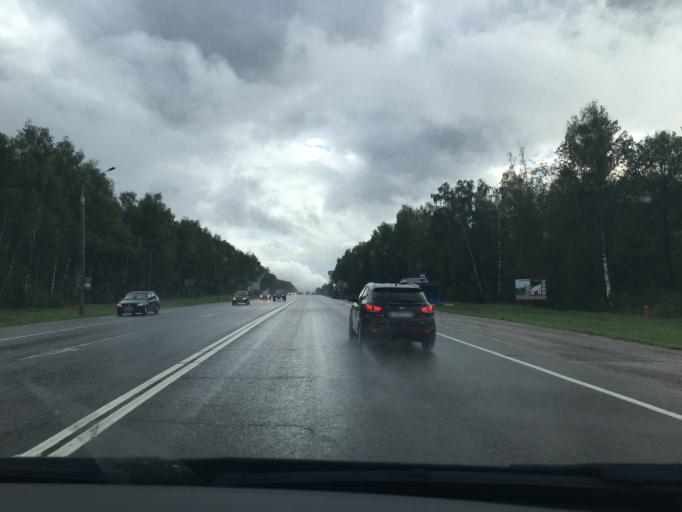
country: RU
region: Kaluga
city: Balabanovo
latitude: 55.1483
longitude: 36.6612
